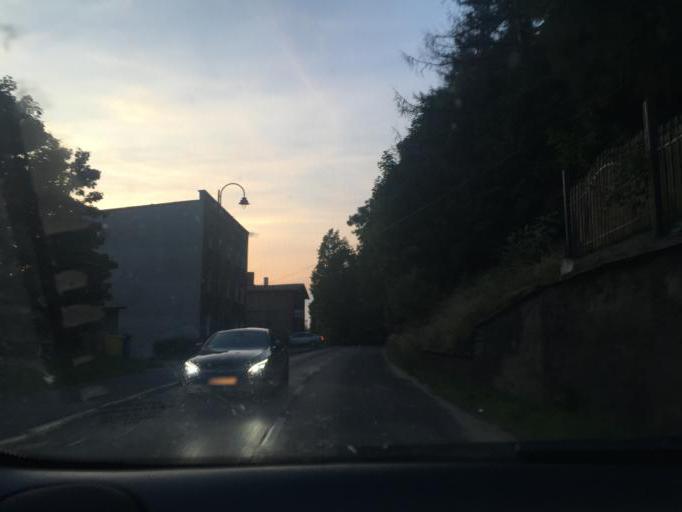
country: PL
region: Lower Silesian Voivodeship
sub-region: Powiat walbrzyski
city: Boguszow-Gorce
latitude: 50.7579
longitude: 16.1992
